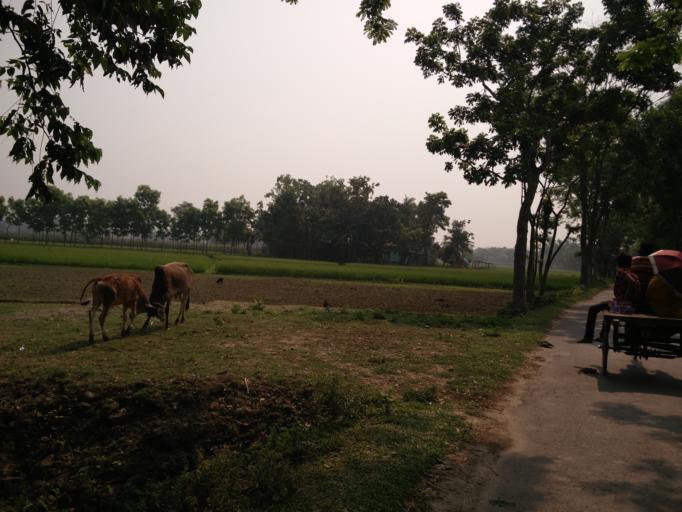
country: BD
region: Dhaka
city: Muktagacha
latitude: 24.9147
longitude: 90.2241
